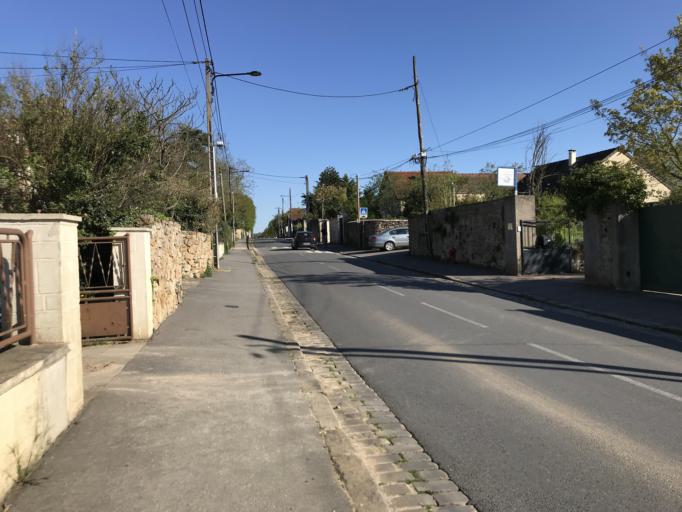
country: FR
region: Ile-de-France
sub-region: Departement de l'Essonne
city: Marcoussis
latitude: 48.6446
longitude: 2.2255
